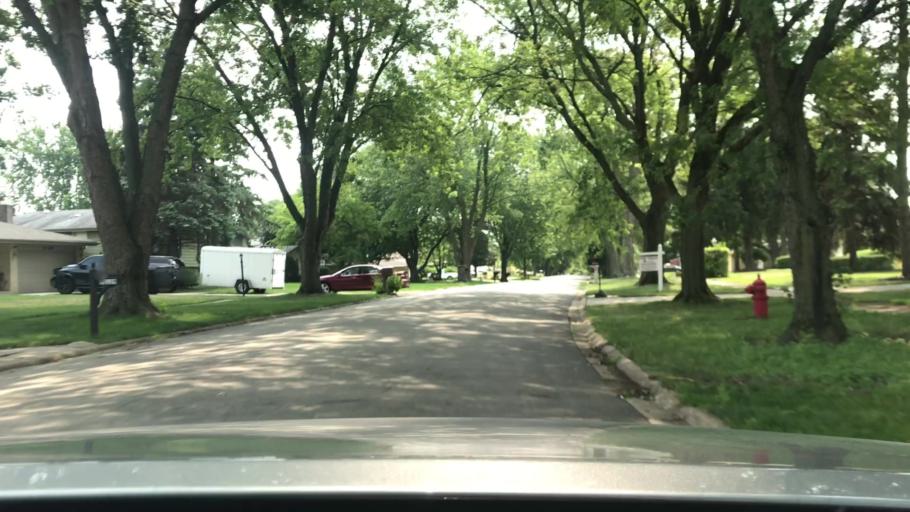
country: US
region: Illinois
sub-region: DuPage County
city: Darien
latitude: 41.7420
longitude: -87.9892
